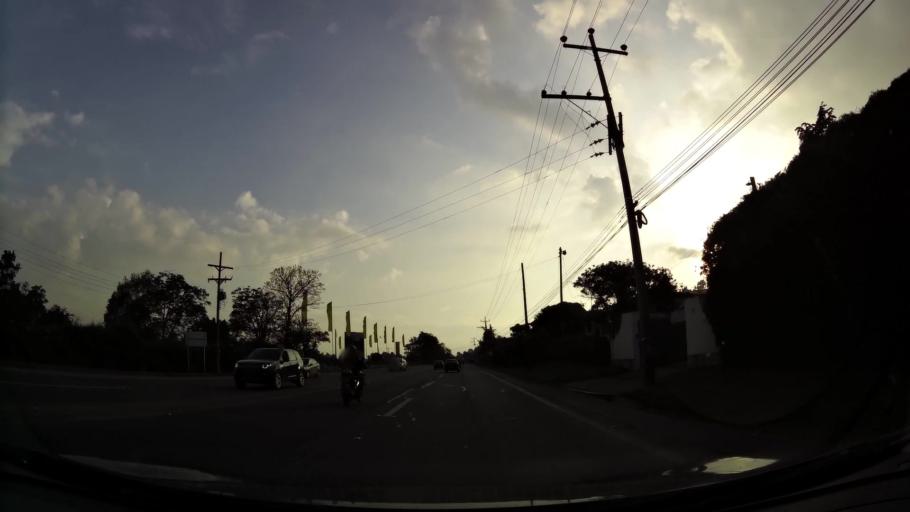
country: CO
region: Cundinamarca
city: Cota
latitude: 4.7876
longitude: -74.1217
